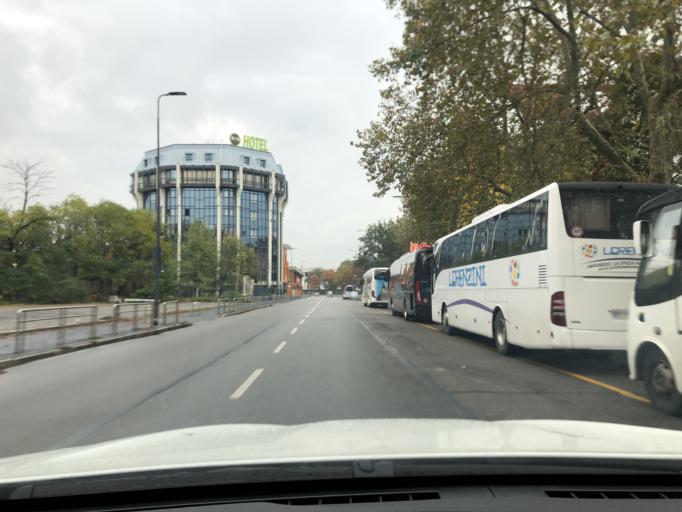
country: IT
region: Lombardy
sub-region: Citta metropolitana di Milano
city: Romano Banco
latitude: 45.4805
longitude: 9.1221
